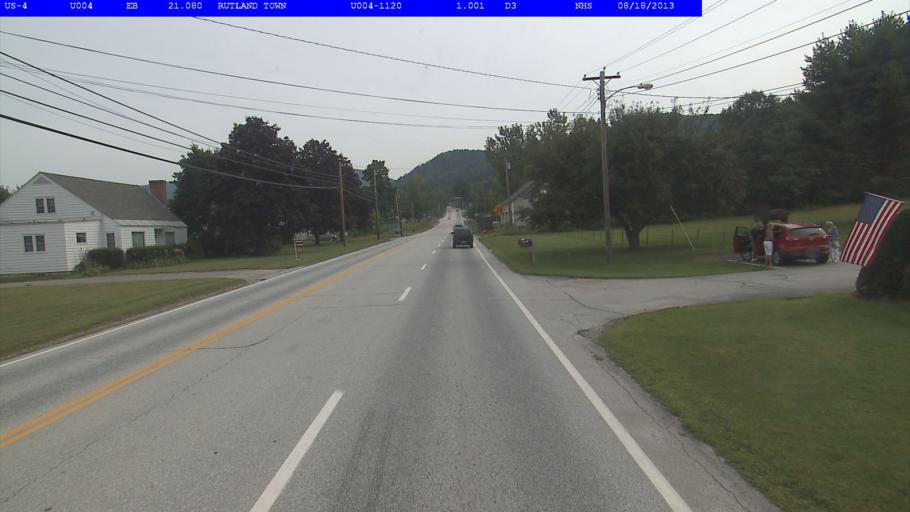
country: US
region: Vermont
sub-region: Rutland County
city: Rutland
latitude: 43.6325
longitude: -72.9408
